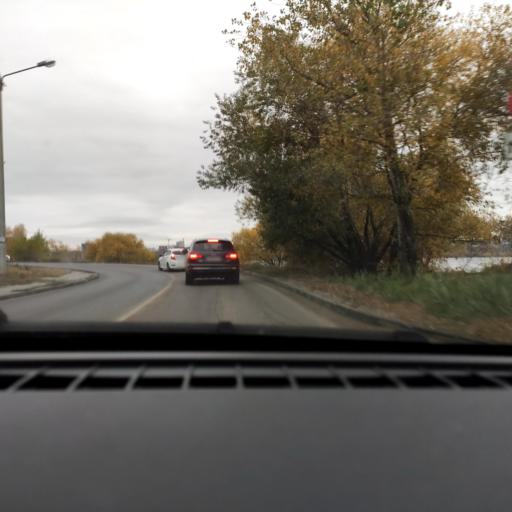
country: RU
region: Voronezj
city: Voronezh
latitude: 51.6979
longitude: 39.2578
